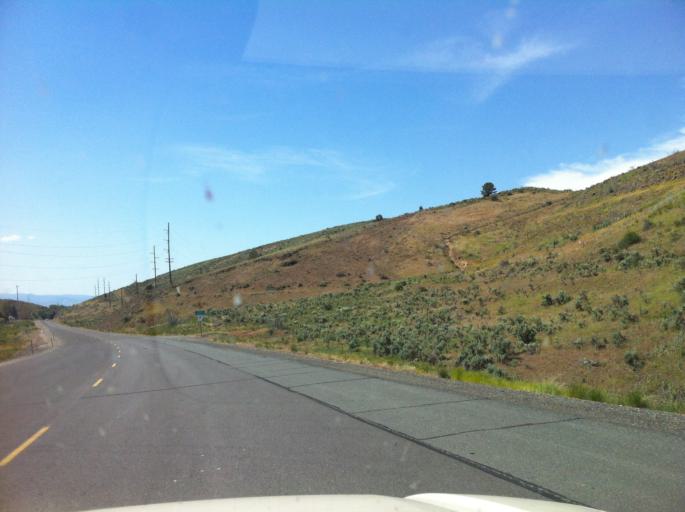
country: US
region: Oregon
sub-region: Baker County
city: Baker City
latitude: 44.7202
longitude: -117.7755
